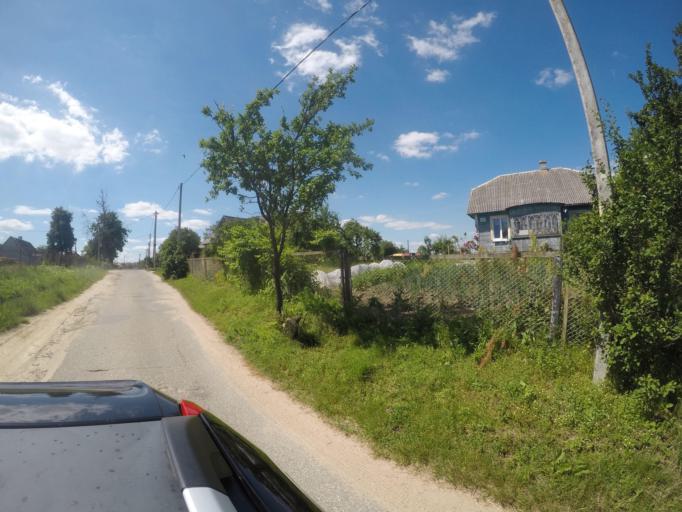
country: BY
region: Grodnenskaya
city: Hrodna
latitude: 53.7259
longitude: 23.8495
